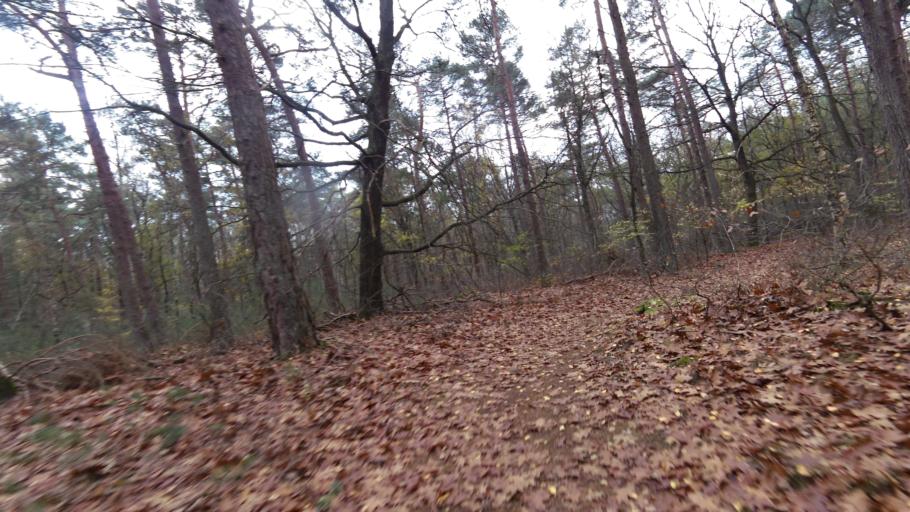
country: NL
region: North Holland
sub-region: Gemeente Hilversum
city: Hilversum
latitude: 52.1982
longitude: 5.1973
